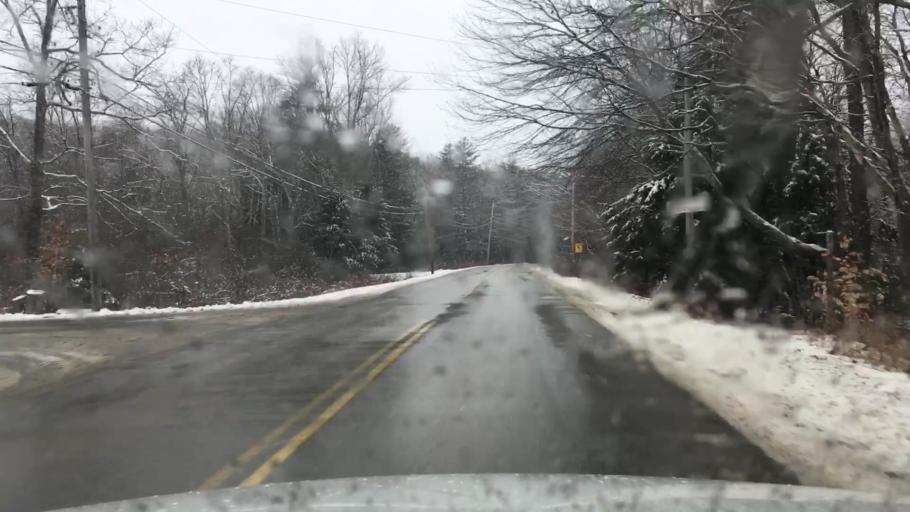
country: US
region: Maine
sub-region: Knox County
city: Warren
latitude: 44.1517
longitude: -69.2811
